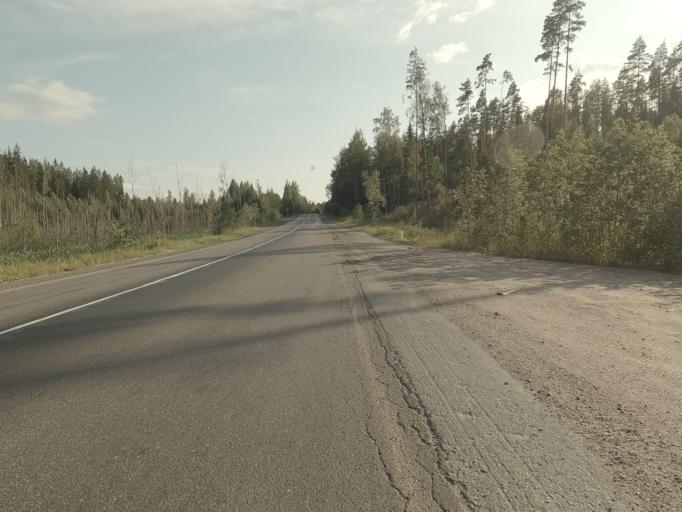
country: RU
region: Leningrad
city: Vyborg
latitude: 60.8489
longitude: 28.8615
